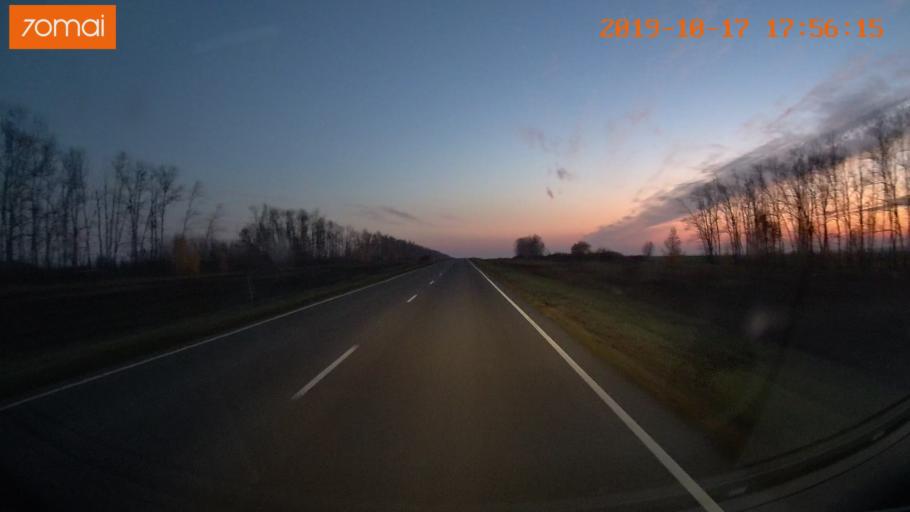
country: RU
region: Tula
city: Kurkino
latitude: 53.5820
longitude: 38.6488
